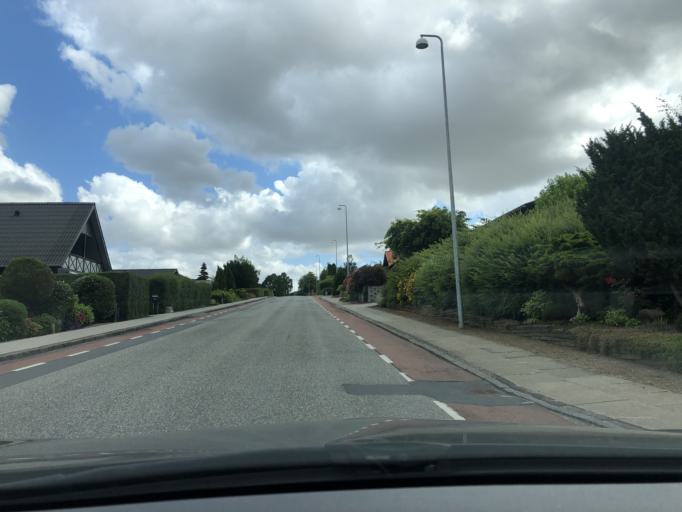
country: DK
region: South Denmark
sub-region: Vejle Kommune
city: Vejle
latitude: 55.6964
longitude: 9.5075
